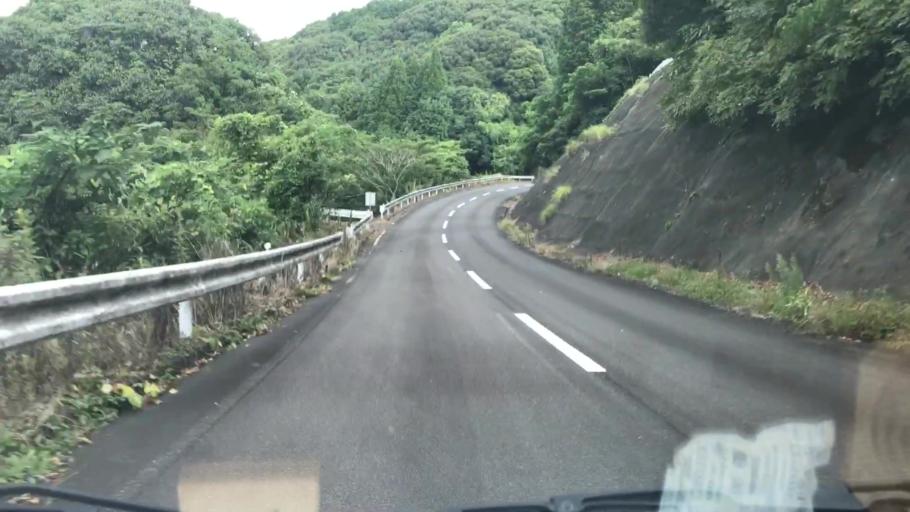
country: JP
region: Saga Prefecture
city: Takeocho-takeo
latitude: 33.2271
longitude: 129.9778
